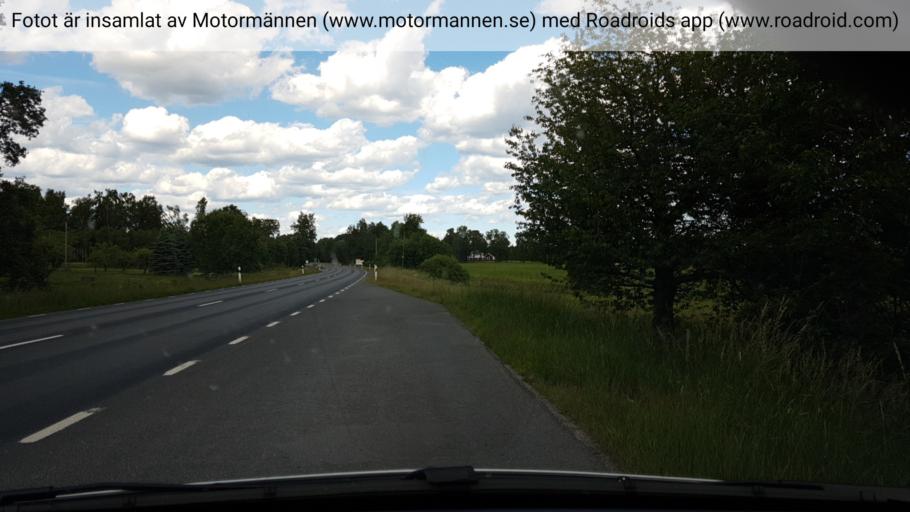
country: SE
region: Vaestra Goetaland
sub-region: Hjo Kommun
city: Hjo
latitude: 58.2626
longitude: 14.2534
